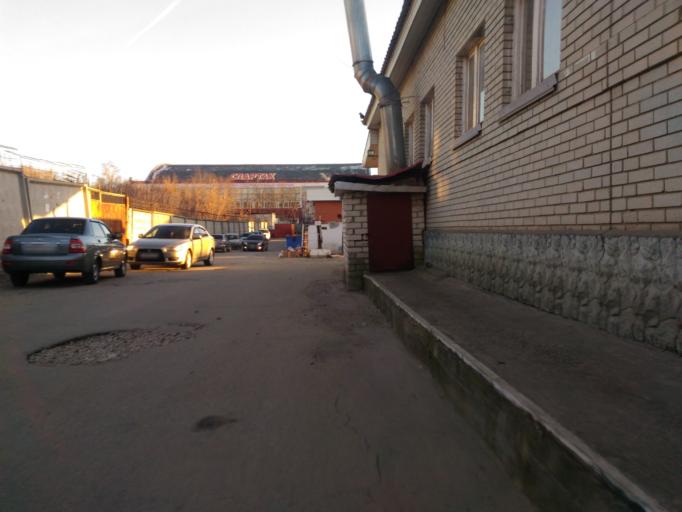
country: RU
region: Ulyanovsk
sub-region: Ulyanovskiy Rayon
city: Ulyanovsk
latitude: 54.3177
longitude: 48.3901
